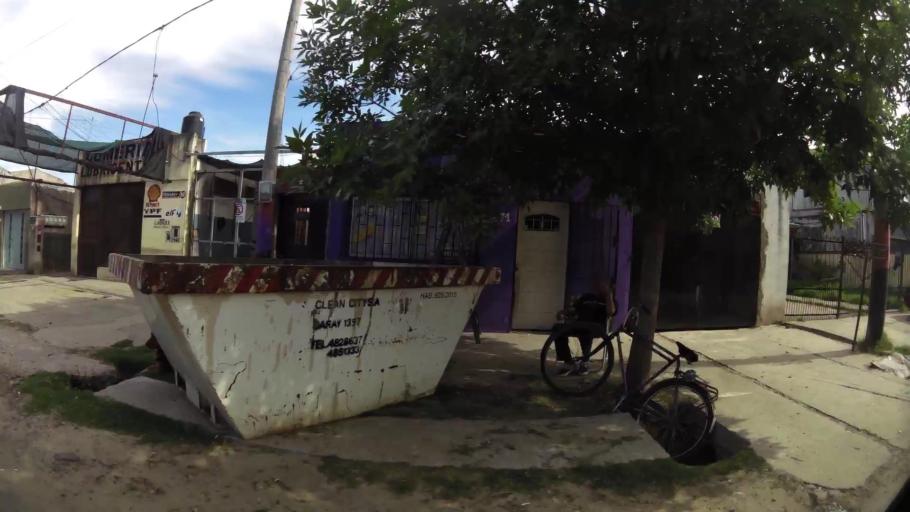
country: AR
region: Santa Fe
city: Granadero Baigorria
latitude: -32.9162
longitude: -60.7186
